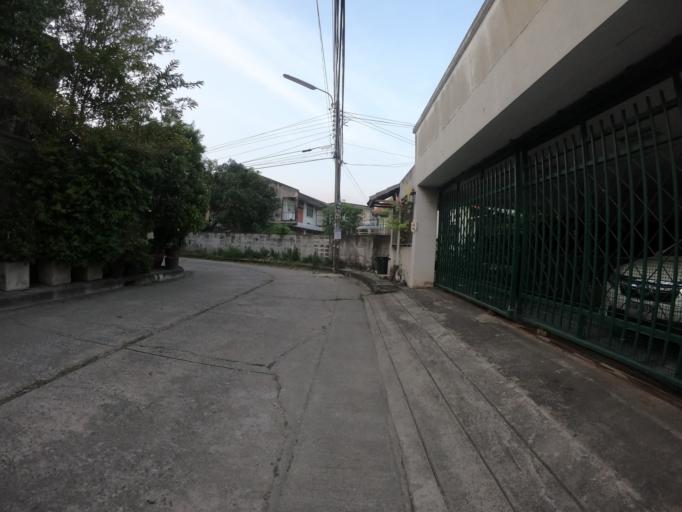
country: TH
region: Bangkok
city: Lat Phrao
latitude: 13.8292
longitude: 100.6067
